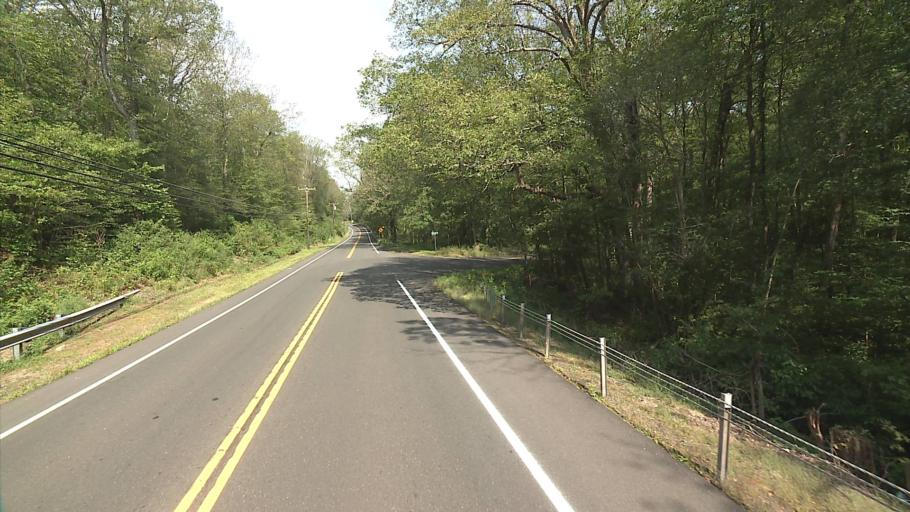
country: US
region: Connecticut
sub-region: Middlesex County
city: Durham
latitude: 41.4058
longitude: -72.6530
